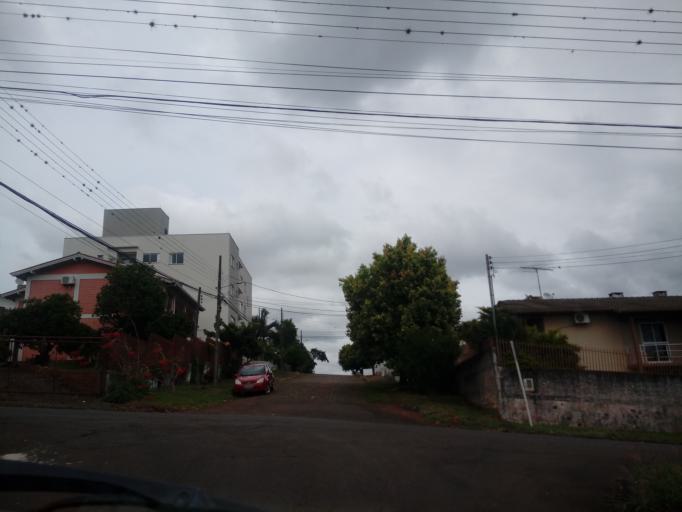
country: BR
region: Santa Catarina
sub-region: Chapeco
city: Chapeco
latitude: -27.0747
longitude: -52.6188
